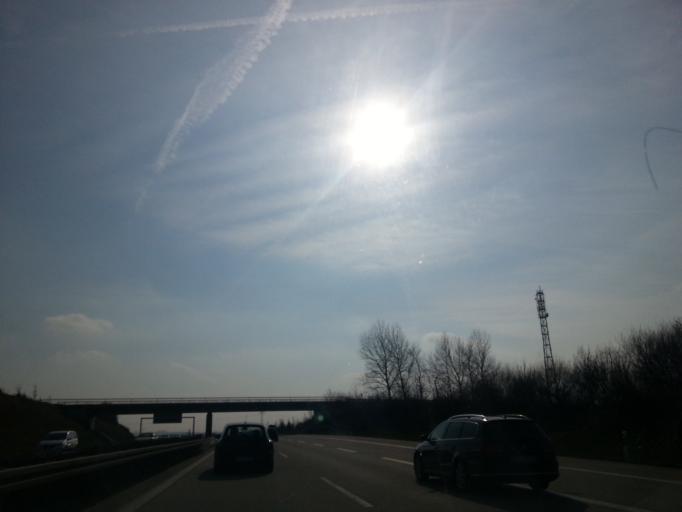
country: DE
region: Saxony
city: Wilsdruff
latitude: 51.0555
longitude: 13.6046
